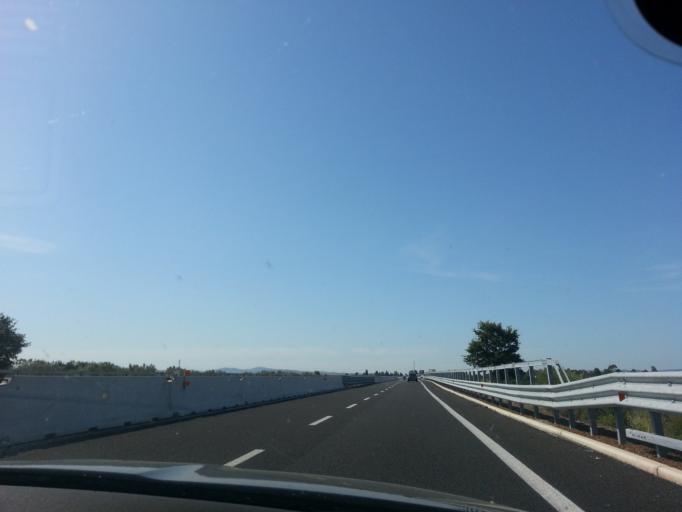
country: IT
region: Latium
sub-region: Provincia di Viterbo
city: Blera
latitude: 42.3343
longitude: 11.9842
